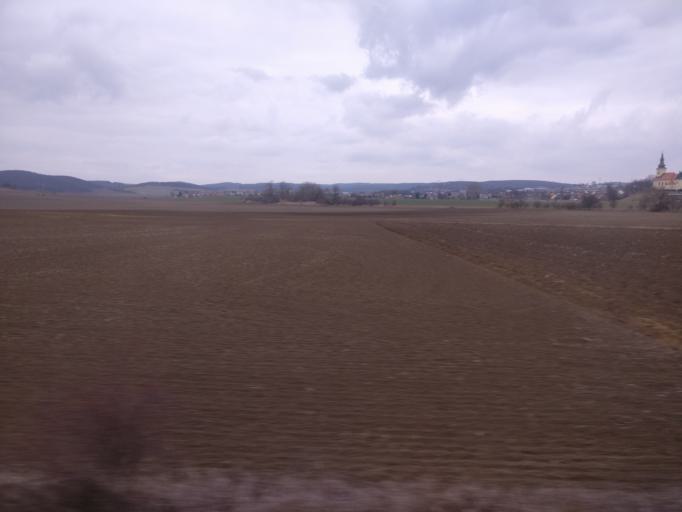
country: CZ
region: South Moravian
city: Troubsko
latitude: 49.1594
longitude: 16.5191
